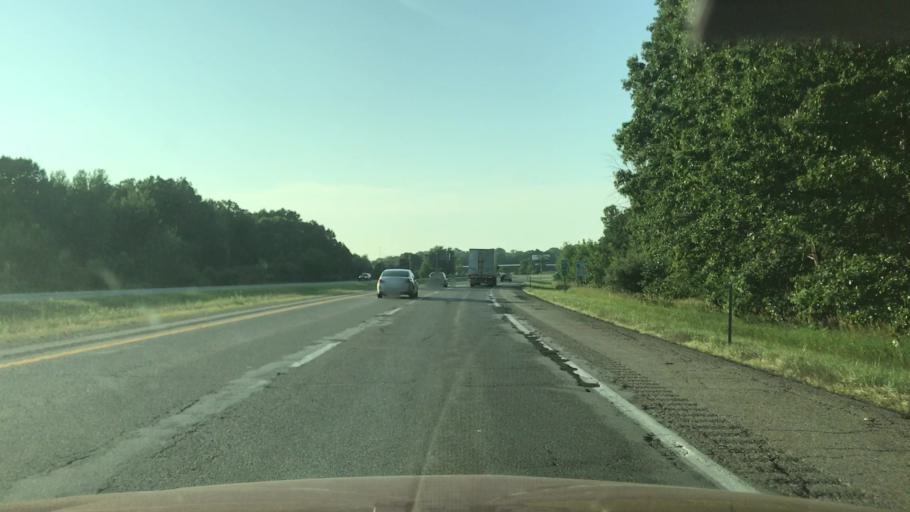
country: US
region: Michigan
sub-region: Berrien County
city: Lake Michigan Beach
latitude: 42.1761
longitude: -86.3779
